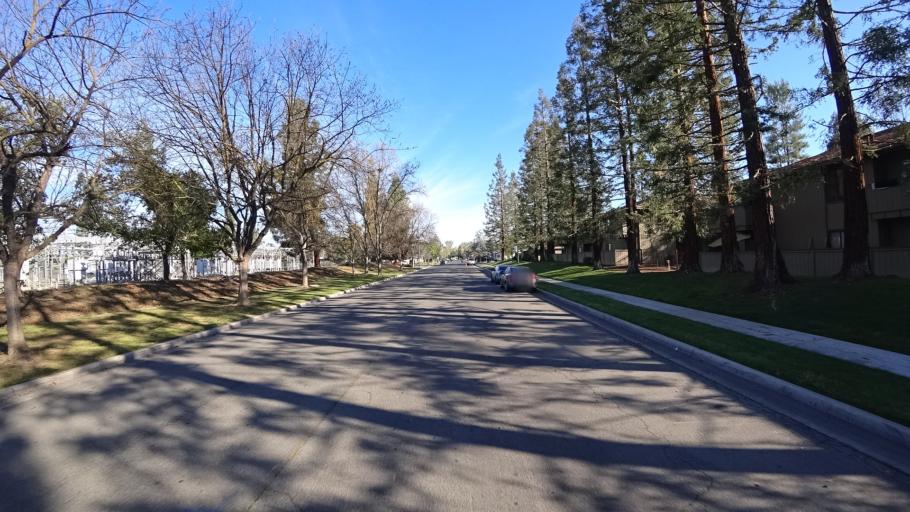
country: US
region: California
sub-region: Fresno County
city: West Park
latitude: 36.8215
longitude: -119.8580
